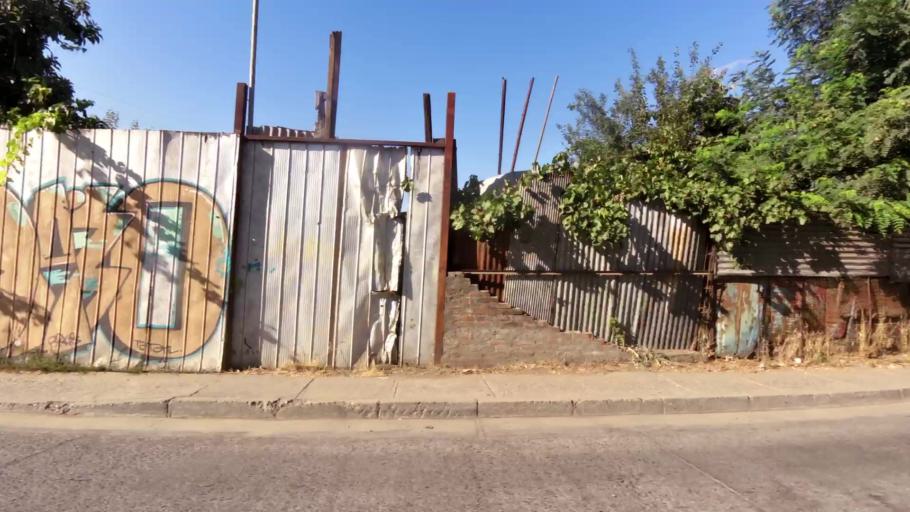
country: CL
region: Maule
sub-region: Provincia de Curico
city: Curico
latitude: -34.9875
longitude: -71.2524
